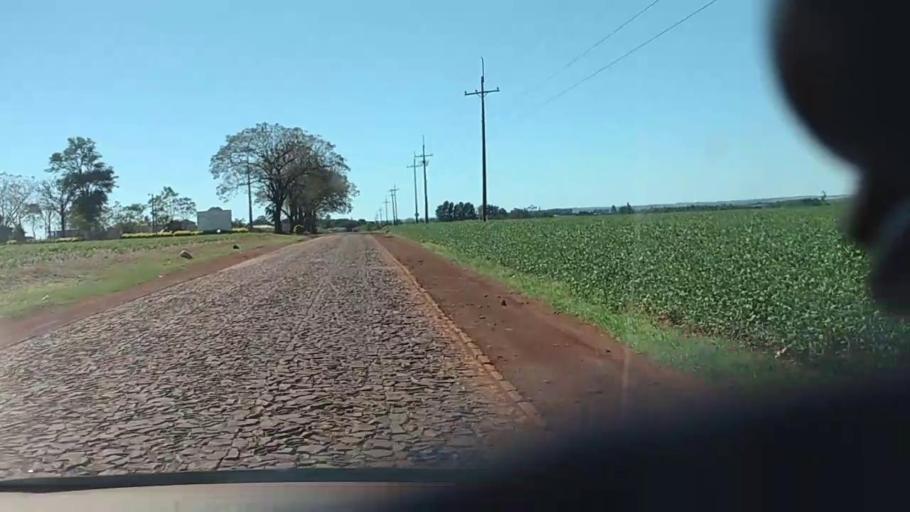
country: PY
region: Alto Parana
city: Naranjal
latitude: -25.9553
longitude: -55.1342
